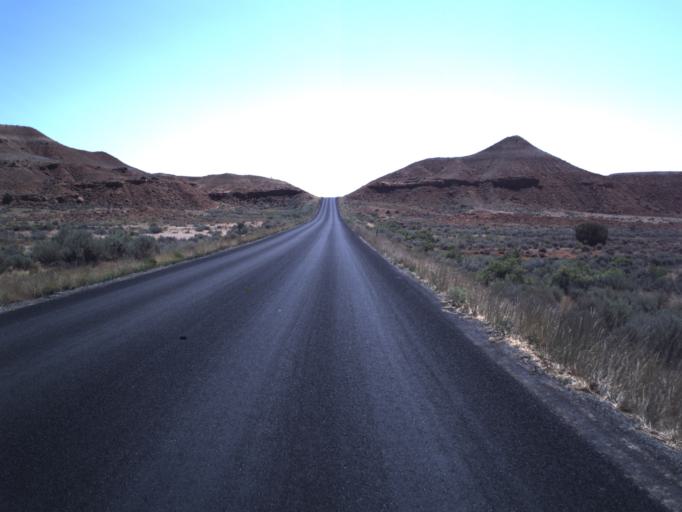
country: US
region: Utah
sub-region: Uintah County
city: Maeser
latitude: 40.4159
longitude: -109.7567
